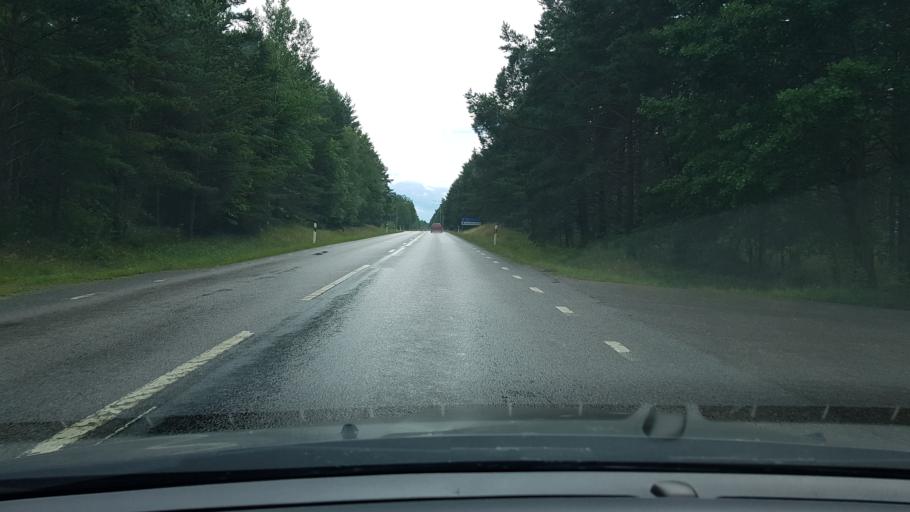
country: SE
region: Uppsala
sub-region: Uppsala Kommun
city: Saevja
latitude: 59.8065
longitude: 17.6873
